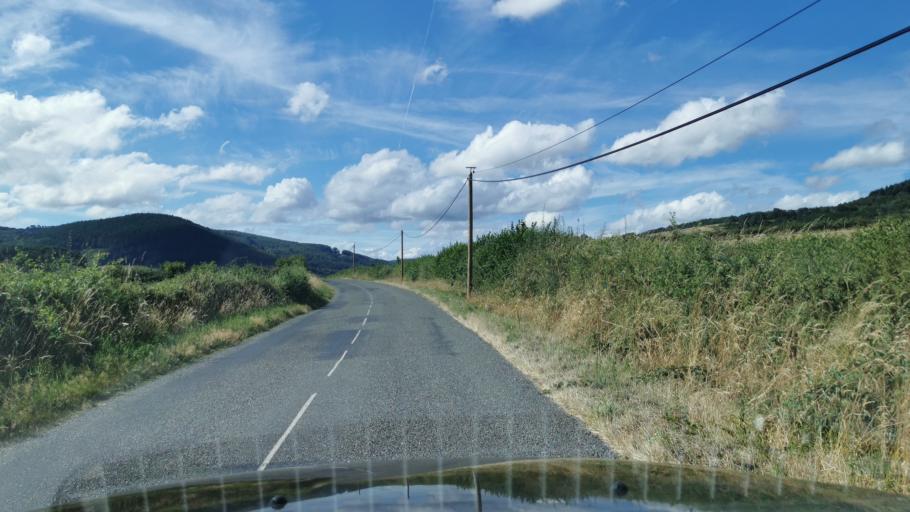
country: FR
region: Bourgogne
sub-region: Departement de Saone-et-Loire
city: Marmagne
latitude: 46.8188
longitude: 4.3266
